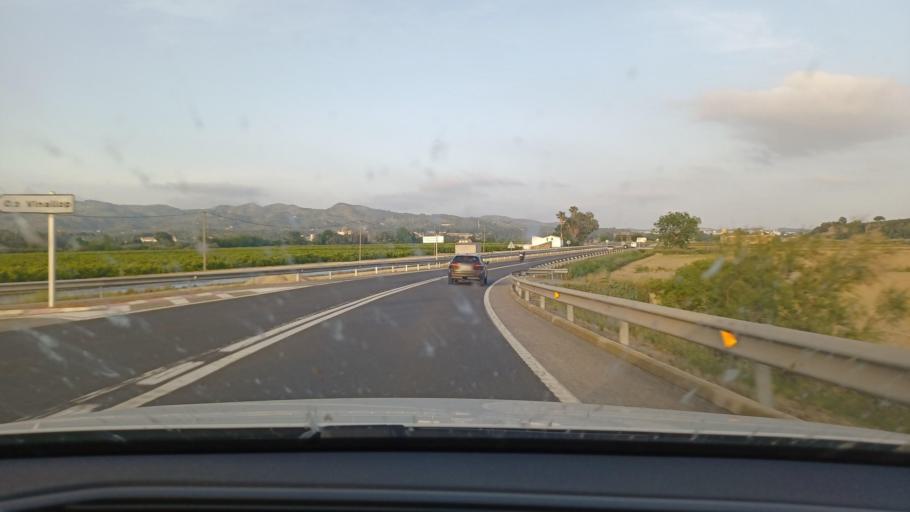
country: ES
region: Catalonia
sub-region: Provincia de Tarragona
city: Tortosa
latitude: 40.7766
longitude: 0.5135
